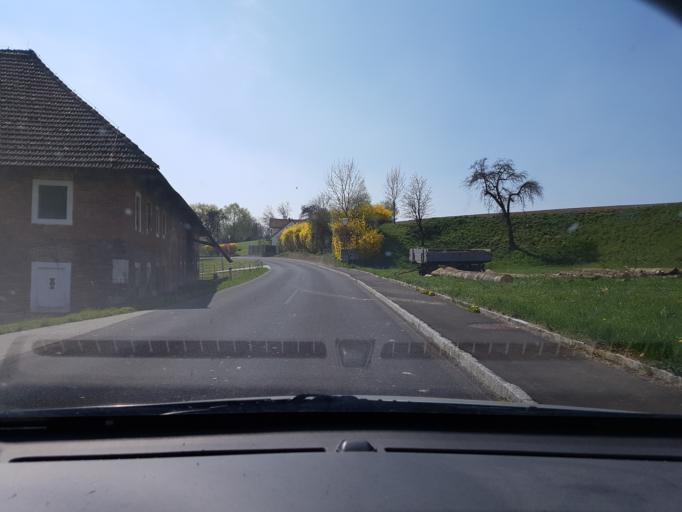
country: AT
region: Upper Austria
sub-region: Politischer Bezirk Linz-Land
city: Sankt Florian
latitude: 48.1960
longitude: 14.3458
